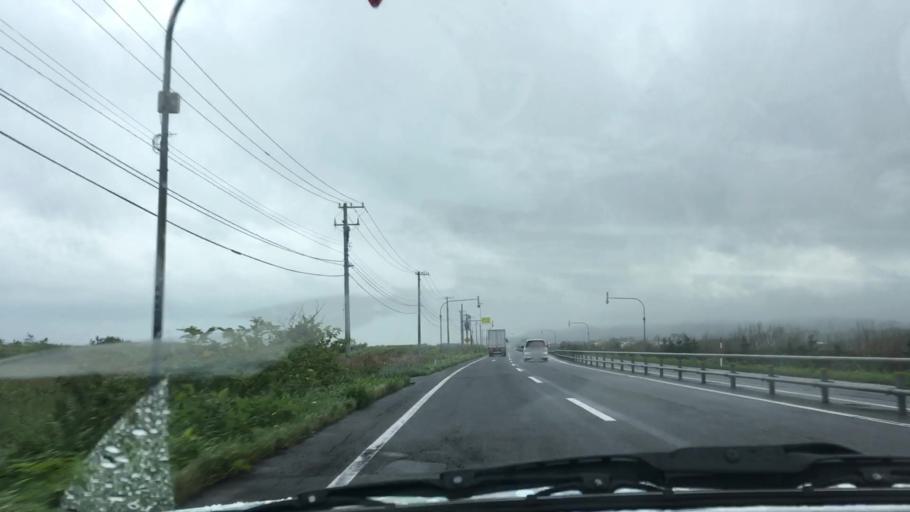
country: JP
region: Hokkaido
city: Niseko Town
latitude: 42.4017
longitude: 140.3037
